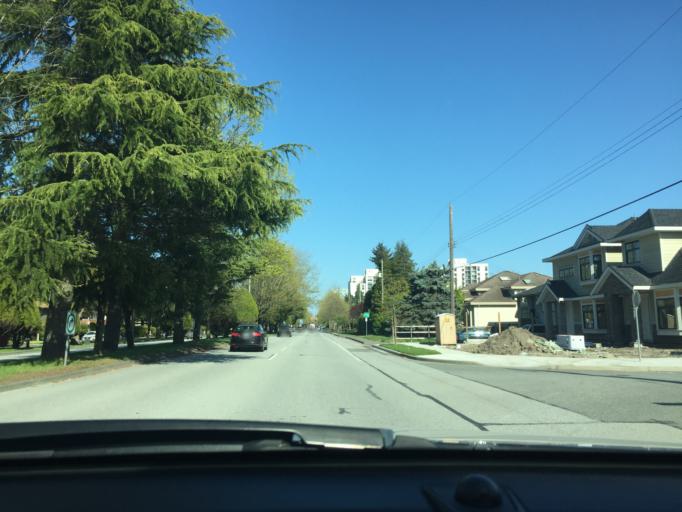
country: CA
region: British Columbia
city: Richmond
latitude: 49.1627
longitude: -123.1524
